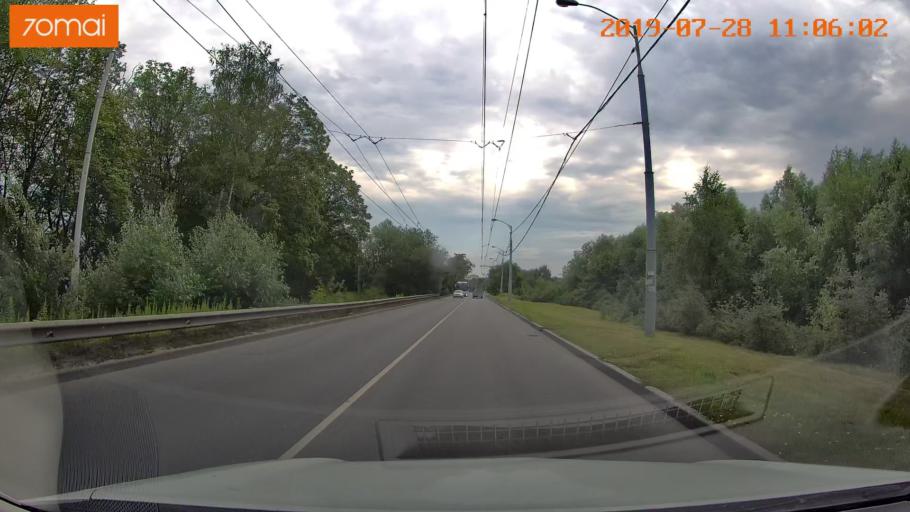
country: RU
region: Kaliningrad
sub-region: Gorod Kaliningrad
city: Kaliningrad
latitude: 54.7157
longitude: 20.4035
